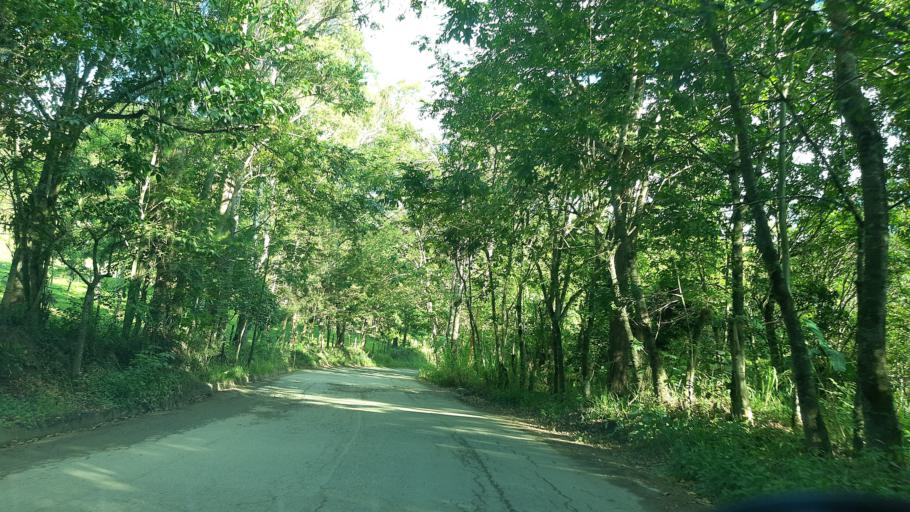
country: CO
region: Boyaca
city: Garagoa
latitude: 5.0753
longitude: -73.3773
